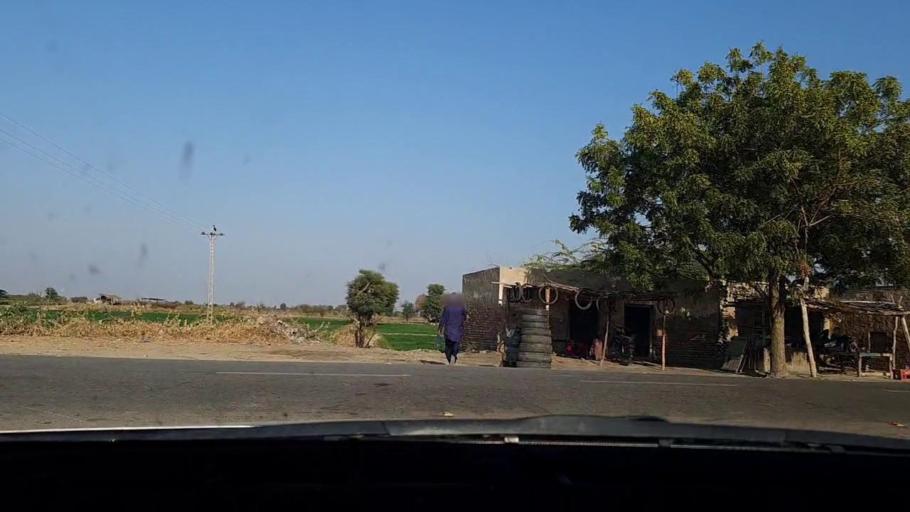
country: PK
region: Sindh
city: Tando Mittha Khan
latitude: 25.8373
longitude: 69.3344
